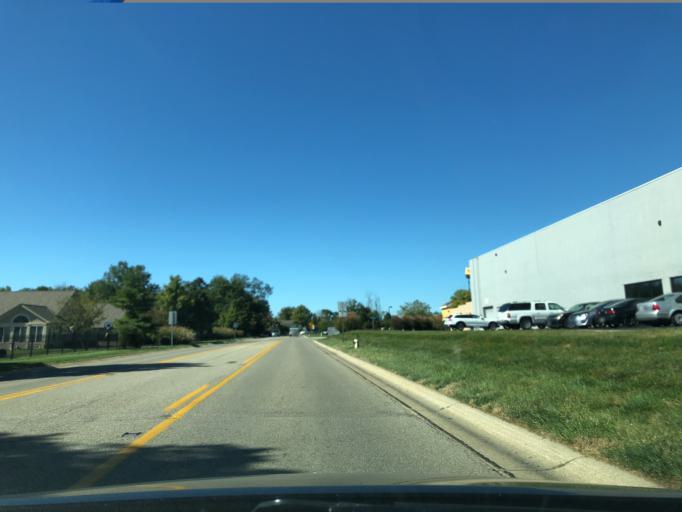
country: US
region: Ohio
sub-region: Hamilton County
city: Sixteen Mile Stand
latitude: 39.2905
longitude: -84.3100
